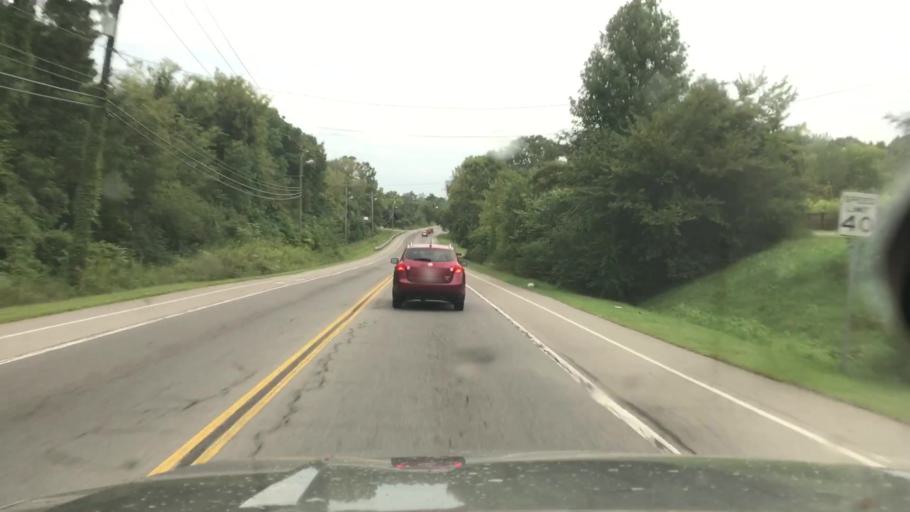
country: US
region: Tennessee
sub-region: Davidson County
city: Lakewood
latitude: 36.1305
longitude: -86.6292
